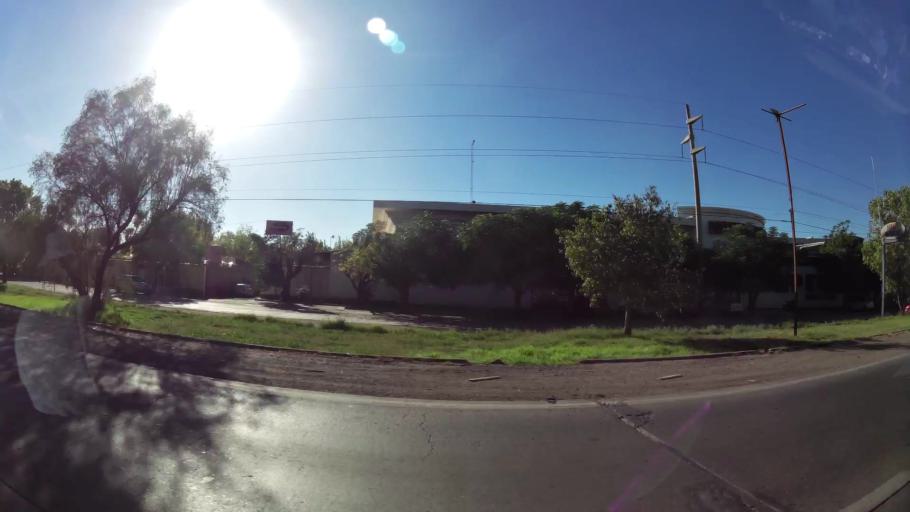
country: AR
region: Mendoza
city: Las Heras
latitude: -32.8536
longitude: -68.8060
